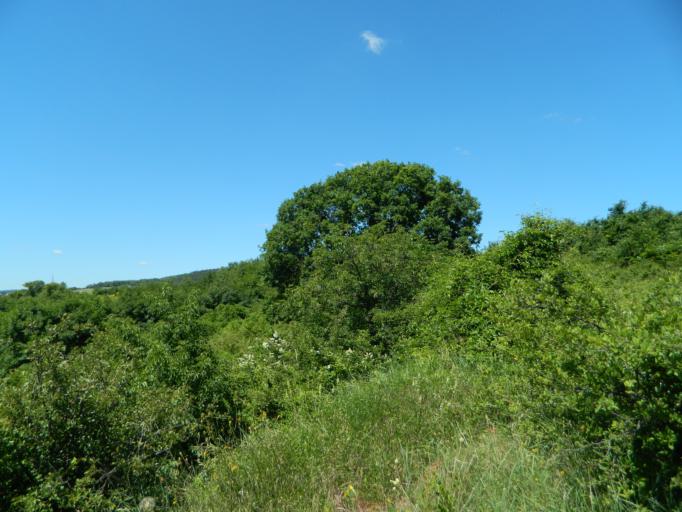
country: HU
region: Pest
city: Budakalasz
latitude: 47.6067
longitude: 19.0342
